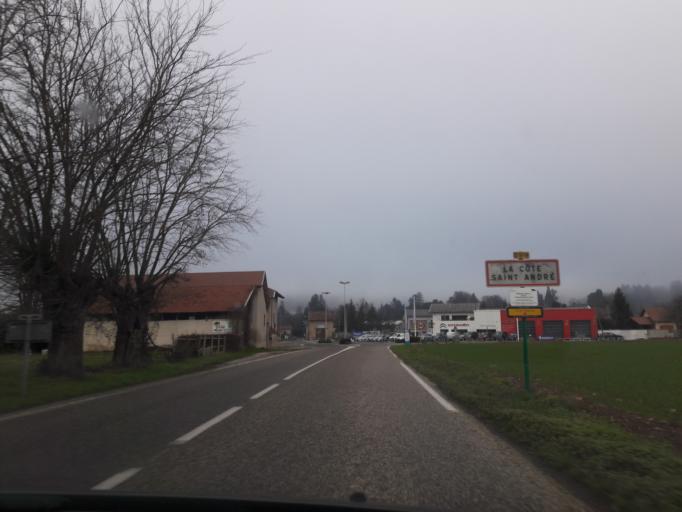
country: FR
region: Rhone-Alpes
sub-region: Departement de l'Isere
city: La Cote-Saint-Andre
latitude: 45.3868
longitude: 5.2723
